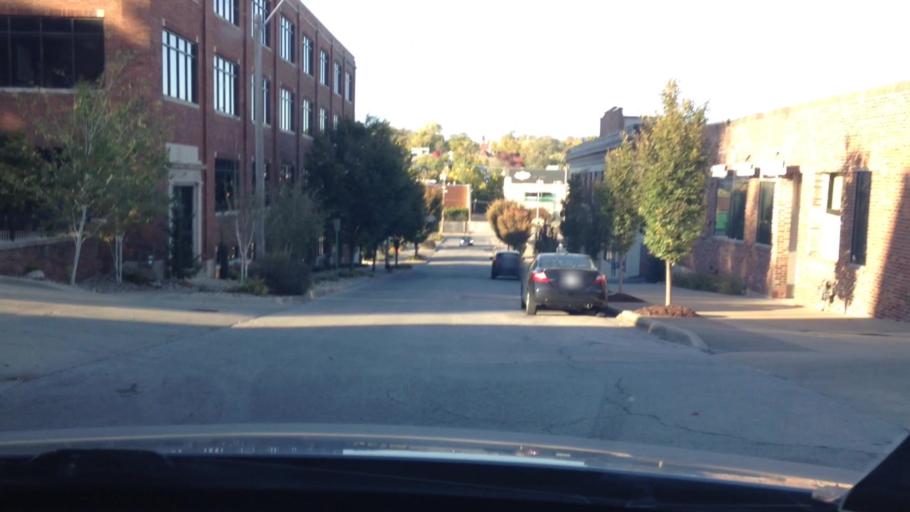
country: US
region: Missouri
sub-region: Jackson County
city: Kansas City
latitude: 39.0806
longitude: -94.5952
